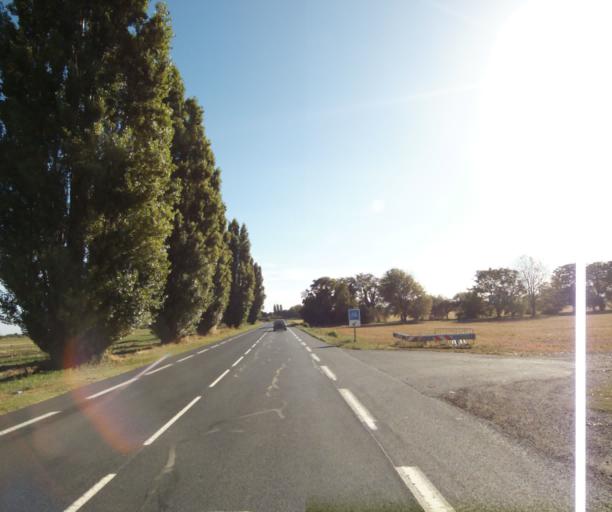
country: FR
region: Auvergne
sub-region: Departement du Puy-de-Dome
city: Aulnat
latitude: 45.8138
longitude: 3.1637
